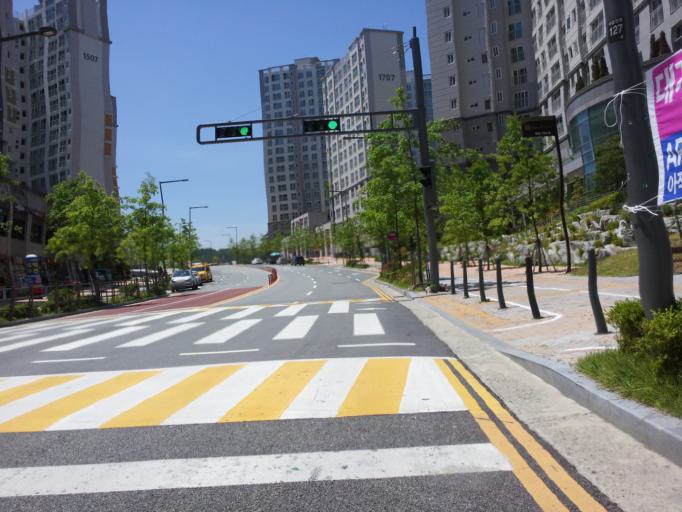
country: KR
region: Chungcheongnam-do
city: Gongju
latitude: 36.5173
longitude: 127.2381
